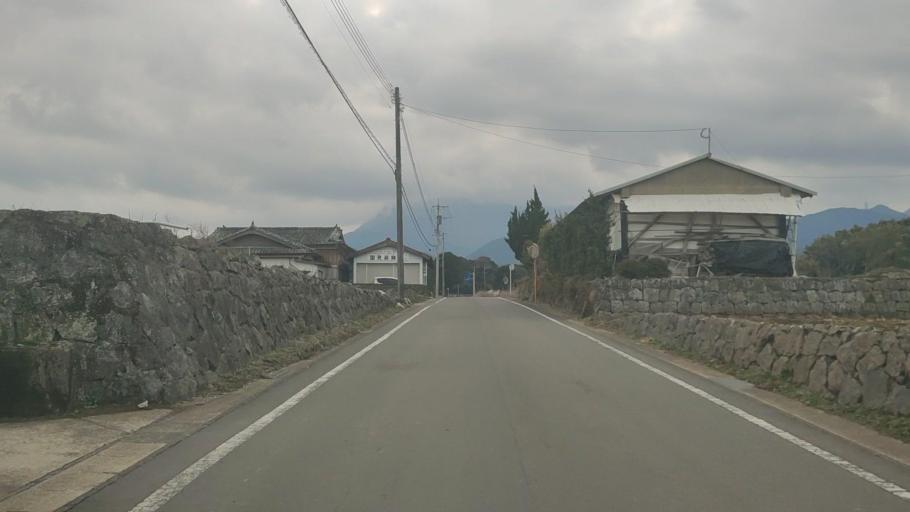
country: JP
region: Nagasaki
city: Shimabara
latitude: 32.8299
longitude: 130.2918
